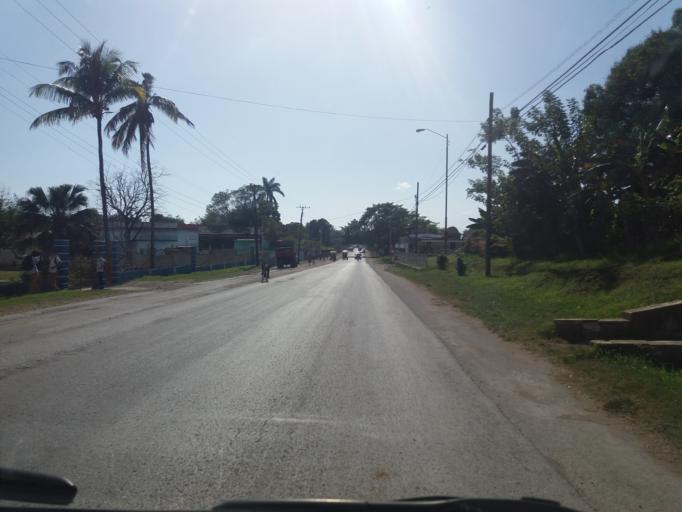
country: CU
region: Cienfuegos
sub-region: Municipio de Cienfuegos
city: Cienfuegos
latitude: 22.1578
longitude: -80.4283
